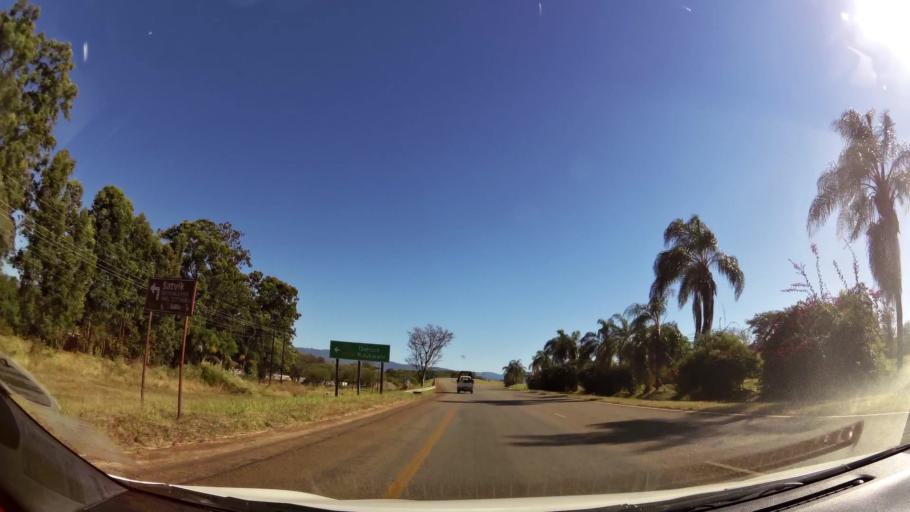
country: ZA
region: Limpopo
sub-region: Mopani District Municipality
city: Tzaneen
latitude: -23.8397
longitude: 30.1394
